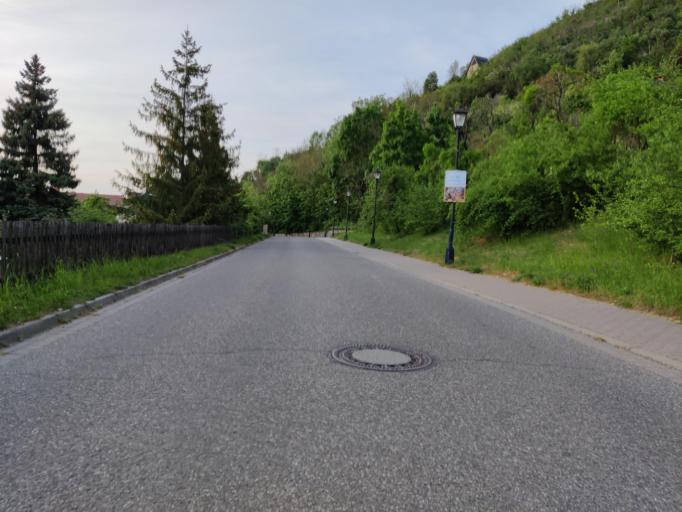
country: DE
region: Saxony-Anhalt
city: Freyburg
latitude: 51.2069
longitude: 11.7730
